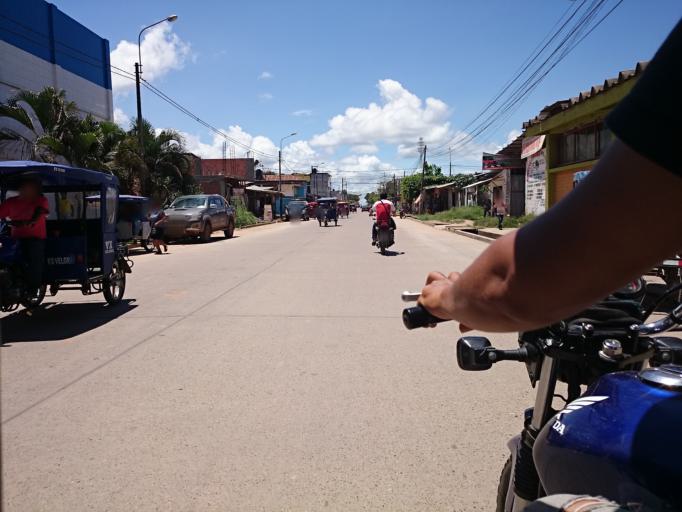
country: PE
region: Ucayali
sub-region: Provincia de Coronel Portillo
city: Pucallpa
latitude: -8.3824
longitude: -74.5410
